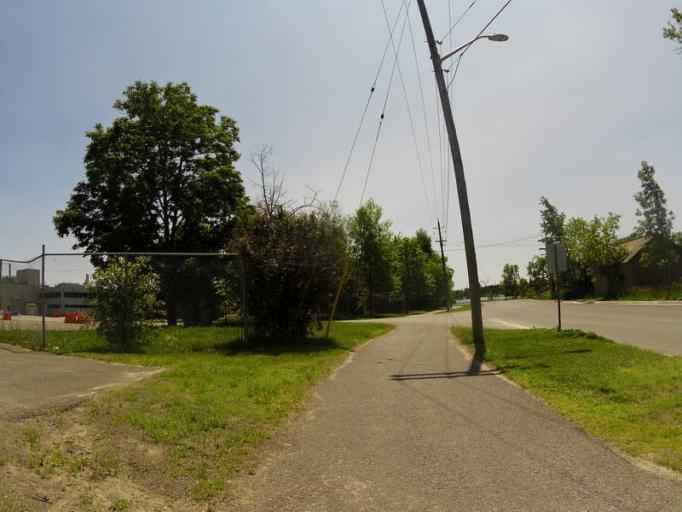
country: CA
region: Ontario
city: Peterborough
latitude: 44.4195
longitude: -78.2680
